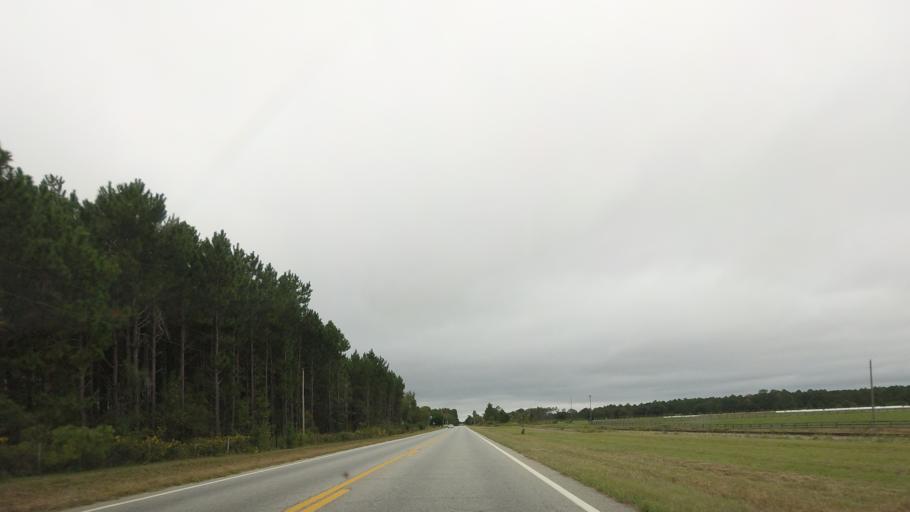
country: US
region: Georgia
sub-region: Berrien County
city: Ray City
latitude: 31.1117
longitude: -83.2104
